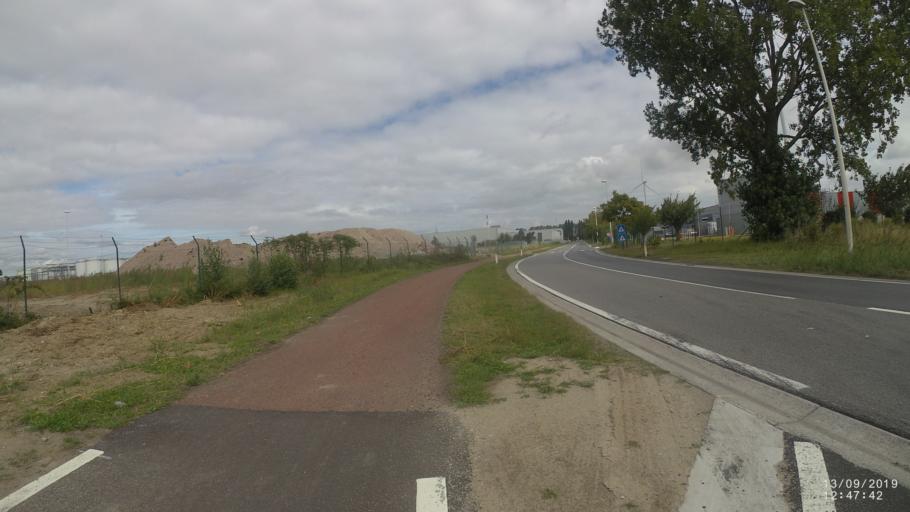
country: BE
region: Flanders
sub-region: Provincie Oost-Vlaanderen
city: Evergem
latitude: 51.1182
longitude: 3.7656
